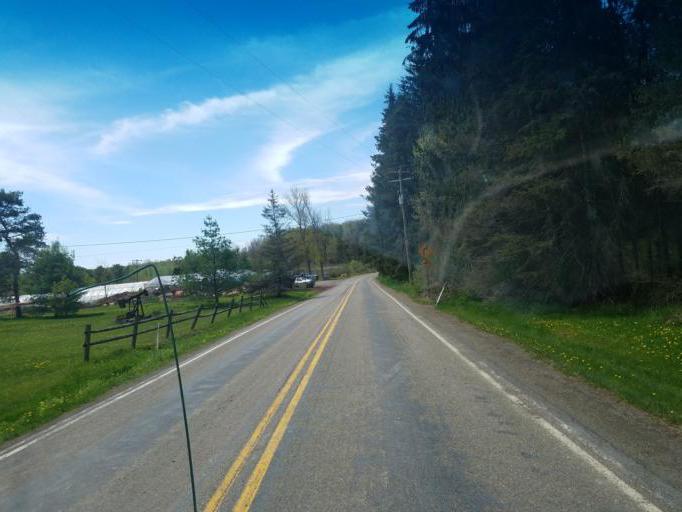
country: US
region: Pennsylvania
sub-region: Tioga County
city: Wellsboro
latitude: 41.6979
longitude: -77.4104
